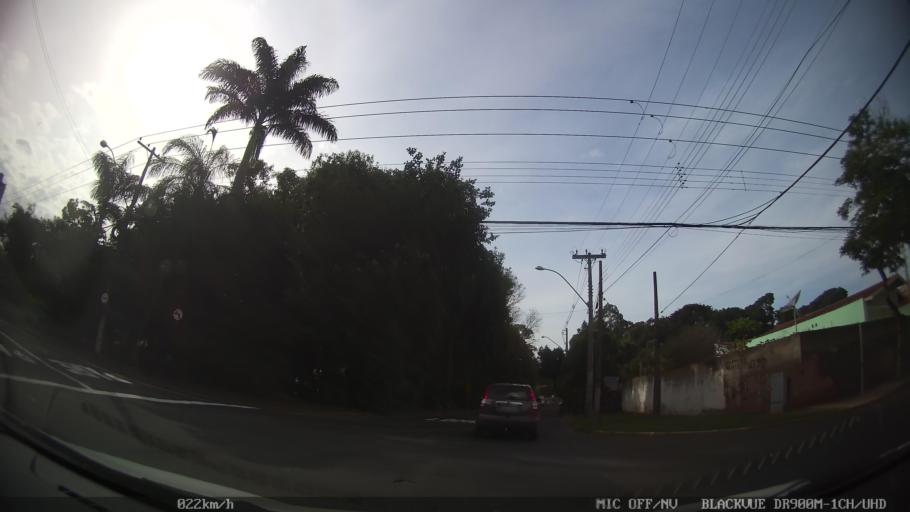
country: BR
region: Sao Paulo
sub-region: Piracicaba
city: Piracicaba
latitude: -22.7197
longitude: -47.6242
